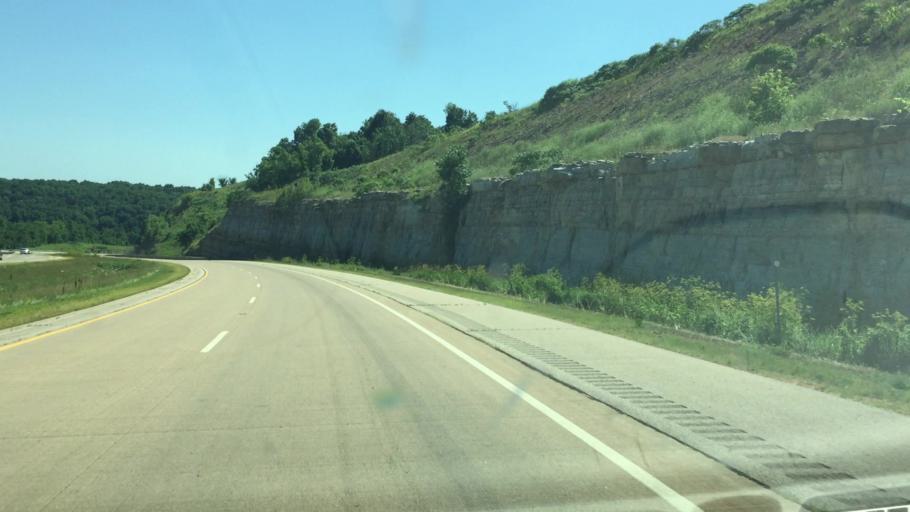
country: US
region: Wisconsin
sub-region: Grant County
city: Dickeyville
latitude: 42.6694
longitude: -90.5506
